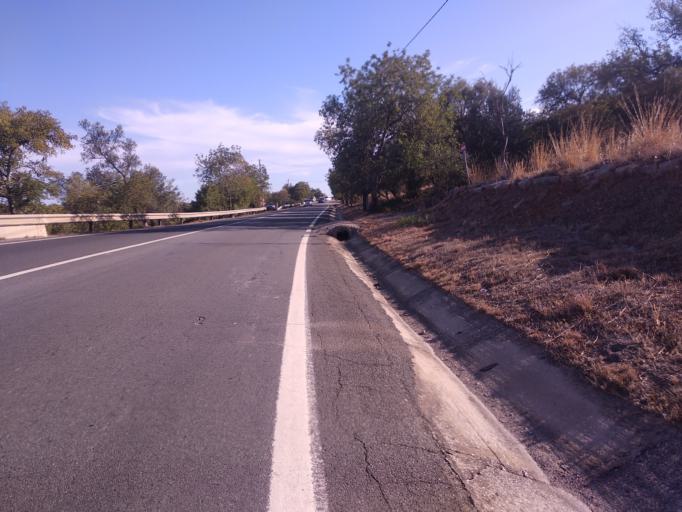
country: PT
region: Faro
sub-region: Sao Bras de Alportel
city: Sao Bras de Alportel
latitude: 37.1034
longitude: -7.9045
